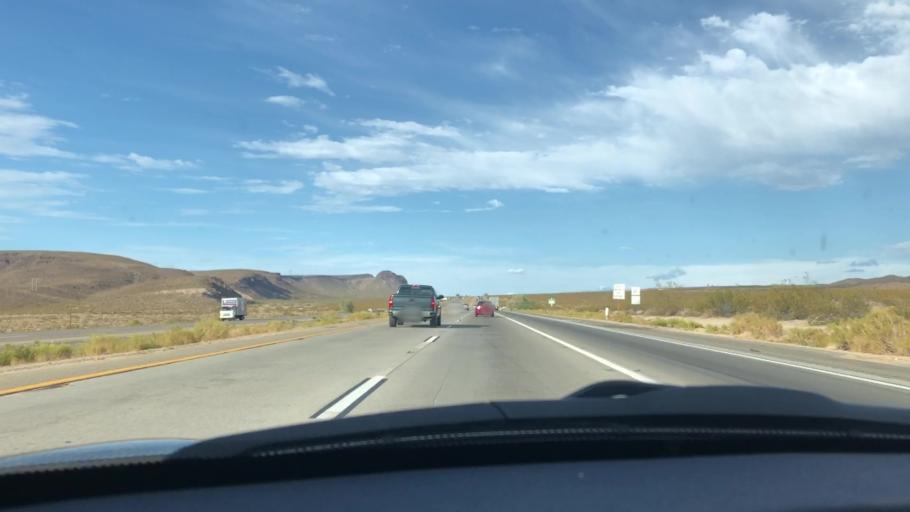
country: US
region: Nevada
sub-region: Clark County
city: Sandy Valley
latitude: 35.3768
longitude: -115.8830
